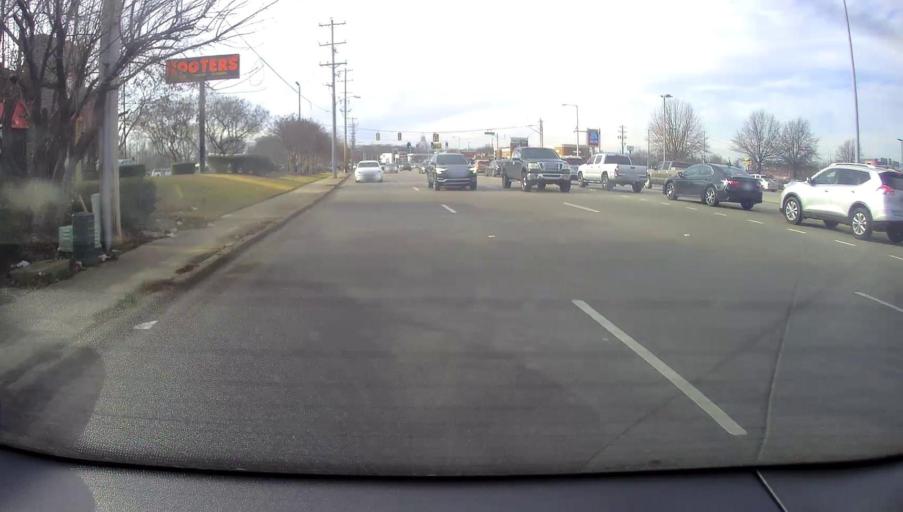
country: US
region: Tennessee
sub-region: Shelby County
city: Germantown
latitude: 35.0502
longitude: -89.8119
